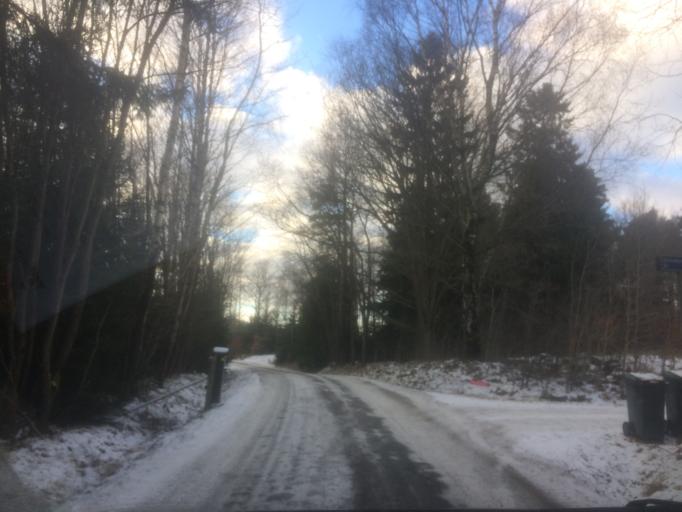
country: SE
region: Vaestra Goetaland
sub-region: Ale Kommun
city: Surte
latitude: 57.8273
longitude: 11.9804
